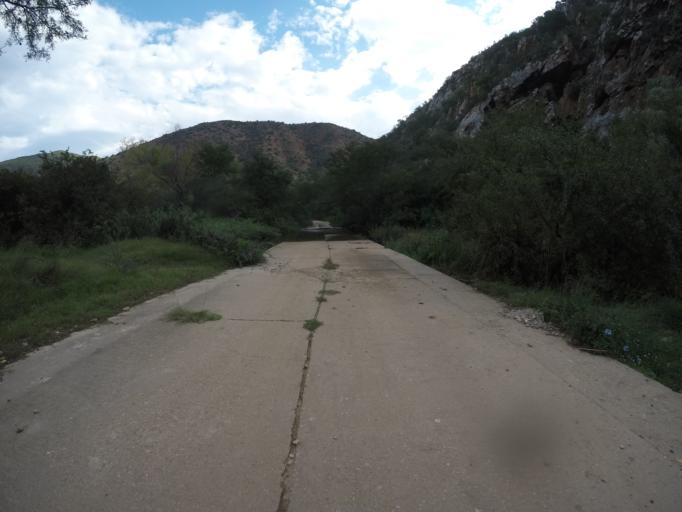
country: ZA
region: Eastern Cape
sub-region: Cacadu District Municipality
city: Kareedouw
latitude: -33.6362
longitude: 24.3182
